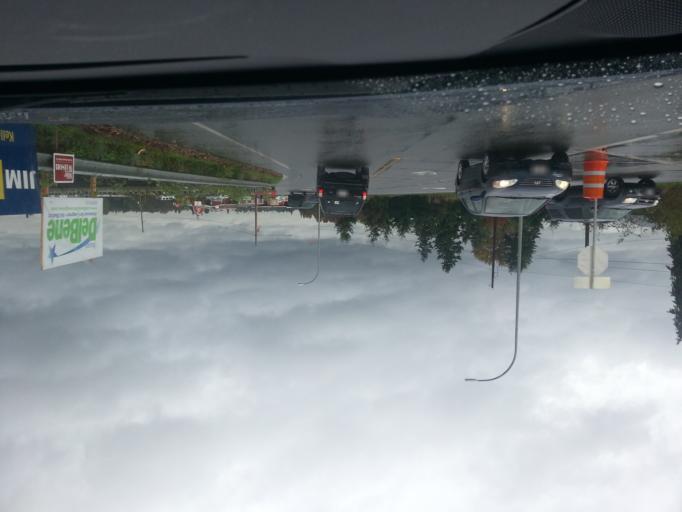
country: US
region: Washington
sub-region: Snohomish County
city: Snohomish
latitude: 47.8989
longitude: -122.1078
